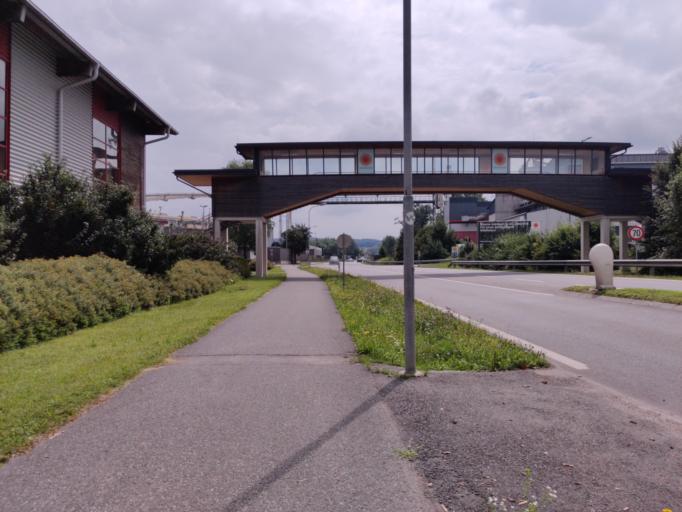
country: AT
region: Lower Austria
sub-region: Politischer Bezirk Melk
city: Ybbs an der Donau
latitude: 48.1668
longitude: 15.0887
